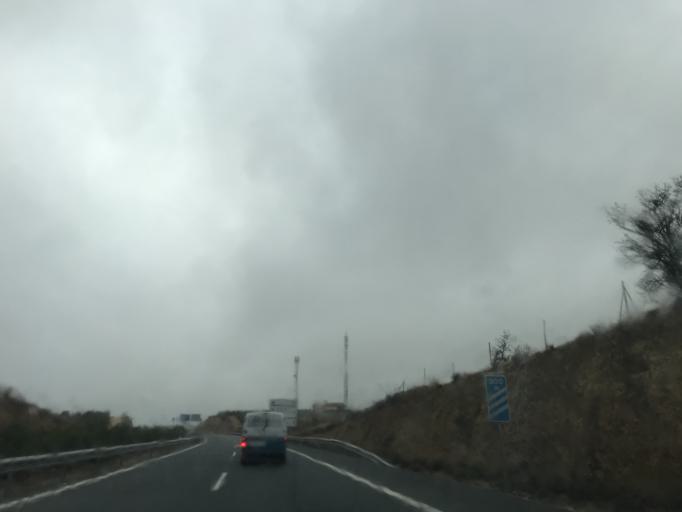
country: ES
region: Andalusia
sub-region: Provincia de Malaga
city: Mollina
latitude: 37.1141
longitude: -4.6606
